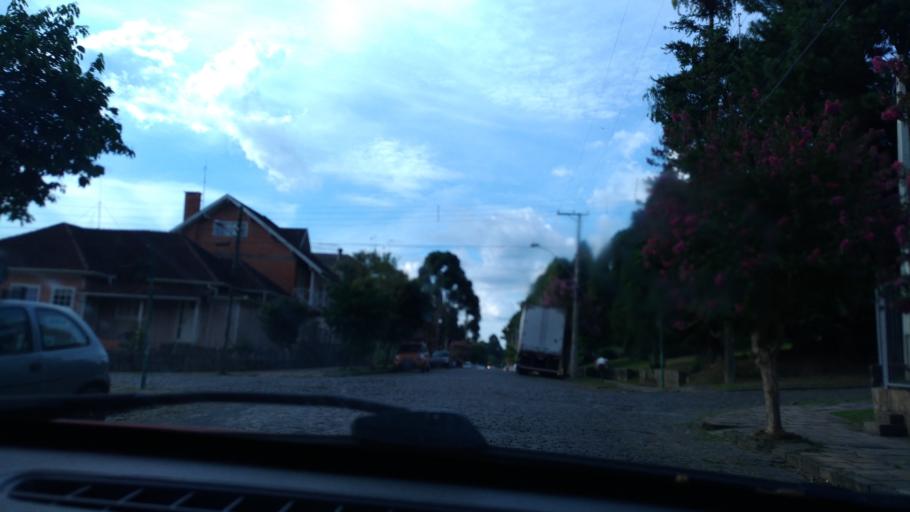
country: BR
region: Rio Grande do Sul
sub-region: Canela
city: Canela
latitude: -29.3577
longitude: -50.8129
